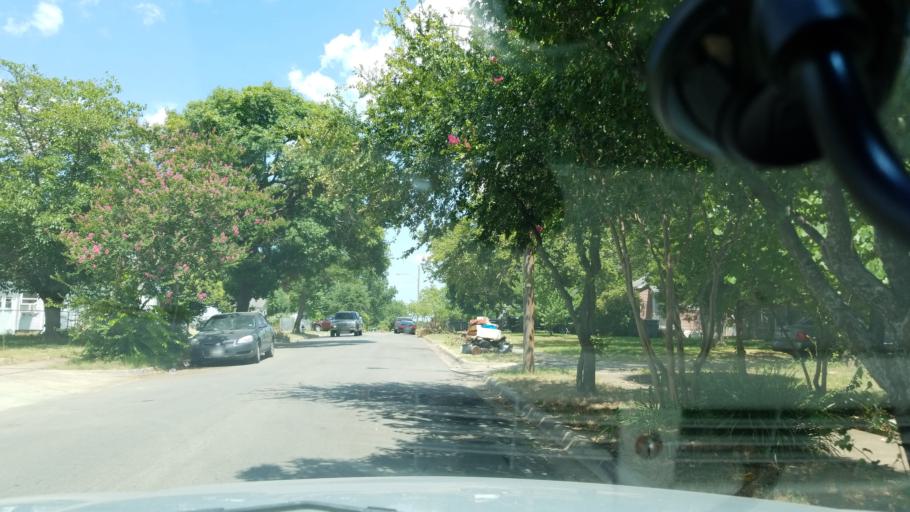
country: US
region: Texas
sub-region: Dallas County
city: Cockrell Hill
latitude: 32.7255
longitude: -96.8765
